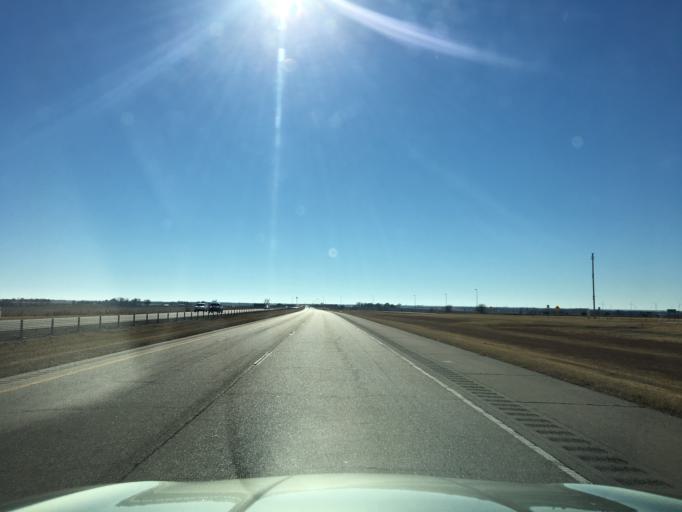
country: US
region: Oklahoma
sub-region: Kay County
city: Blackwell
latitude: 36.9848
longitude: -97.3457
